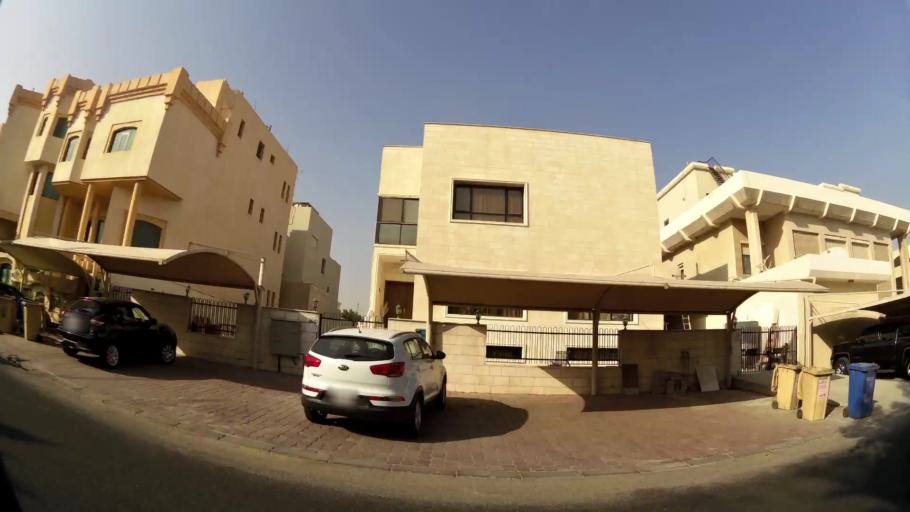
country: KW
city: Bayan
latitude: 29.3128
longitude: 48.0404
